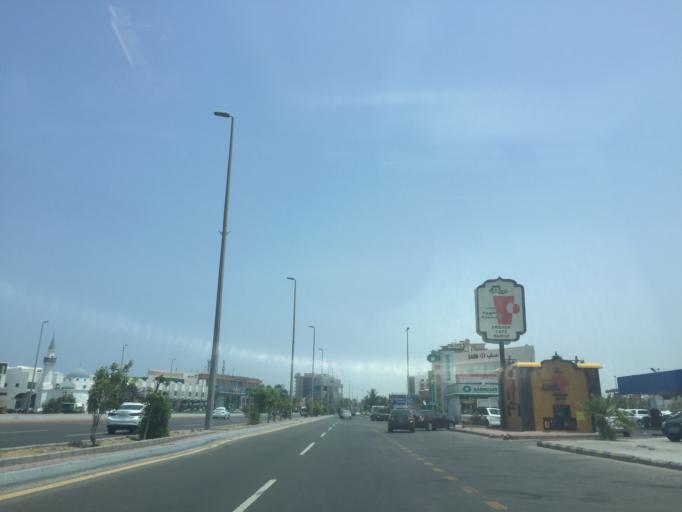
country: SA
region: Makkah
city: Jeddah
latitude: 21.5964
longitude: 39.1226
